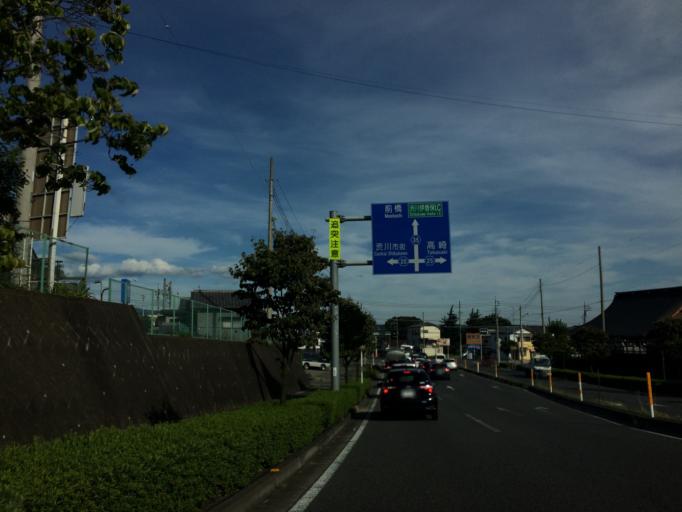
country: JP
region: Gunma
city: Shibukawa
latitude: 36.4837
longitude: 139.0016
